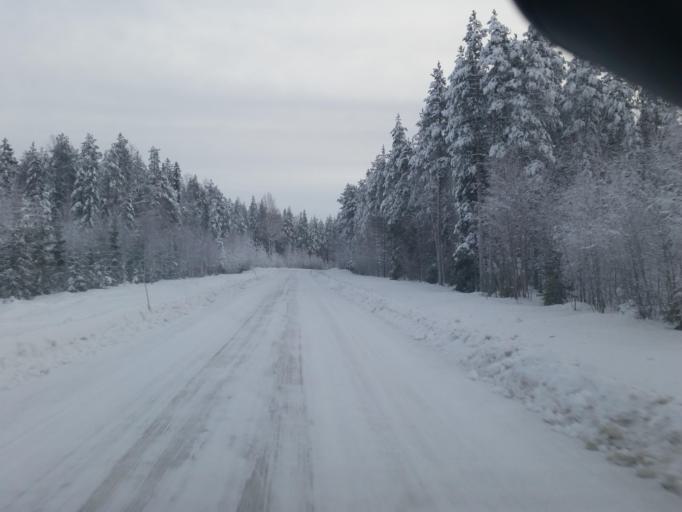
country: SE
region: Norrbotten
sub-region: Pitea Kommun
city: Norrfjarden
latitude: 65.5923
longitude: 21.4525
